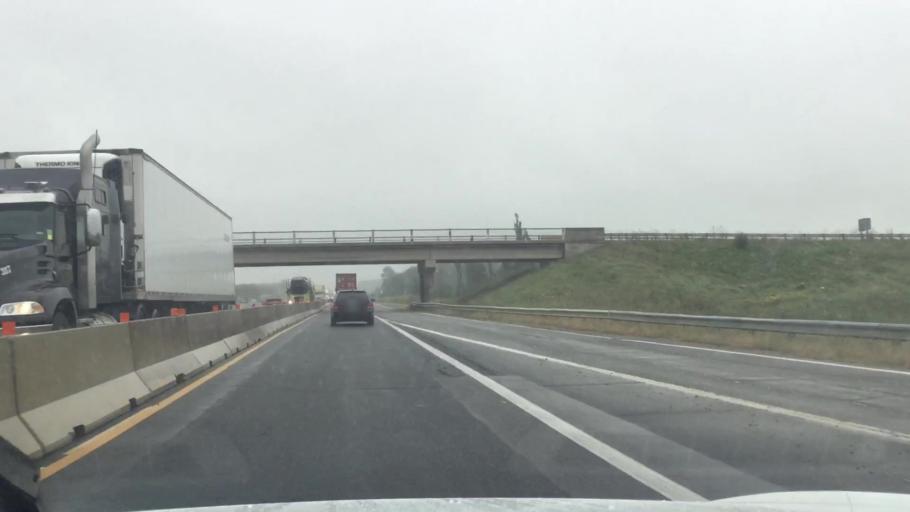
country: CA
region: Ontario
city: Delaware
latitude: 42.7715
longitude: -81.3803
